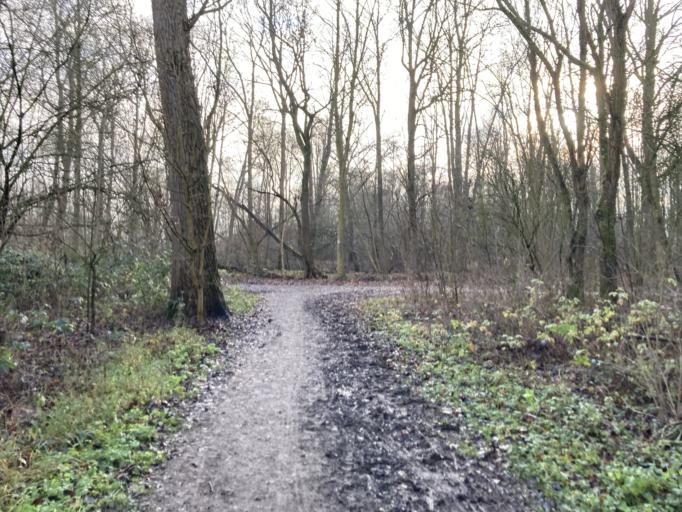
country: DE
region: North Rhine-Westphalia
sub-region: Regierungsbezirk Dusseldorf
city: Neubrueck
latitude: 51.1163
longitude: 6.6152
